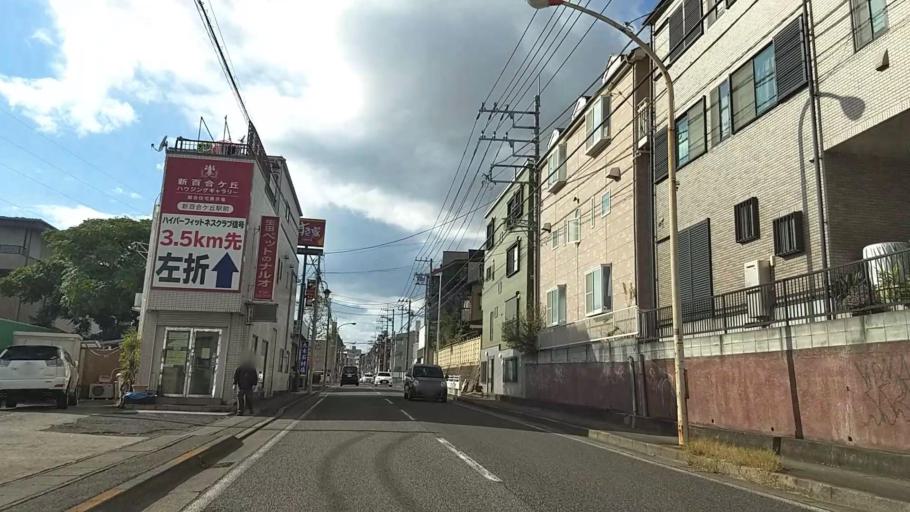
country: JP
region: Tokyo
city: Chofugaoka
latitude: 35.6150
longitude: 139.5356
